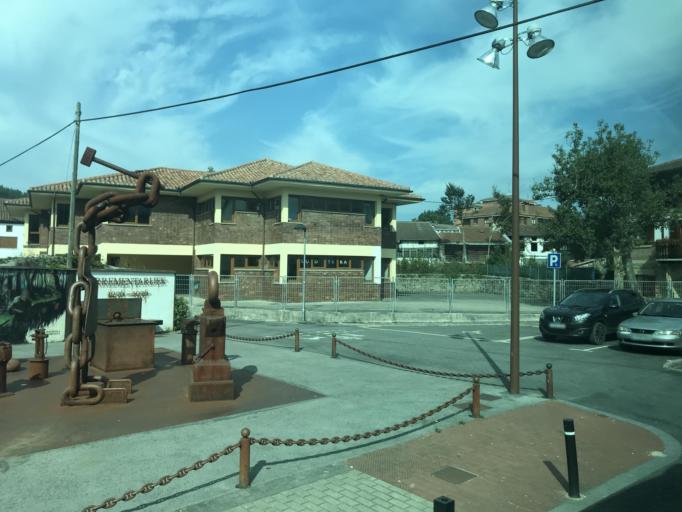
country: ES
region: Basque Country
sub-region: Bizkaia
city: Otxandio
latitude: 43.0414
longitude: -2.6538
